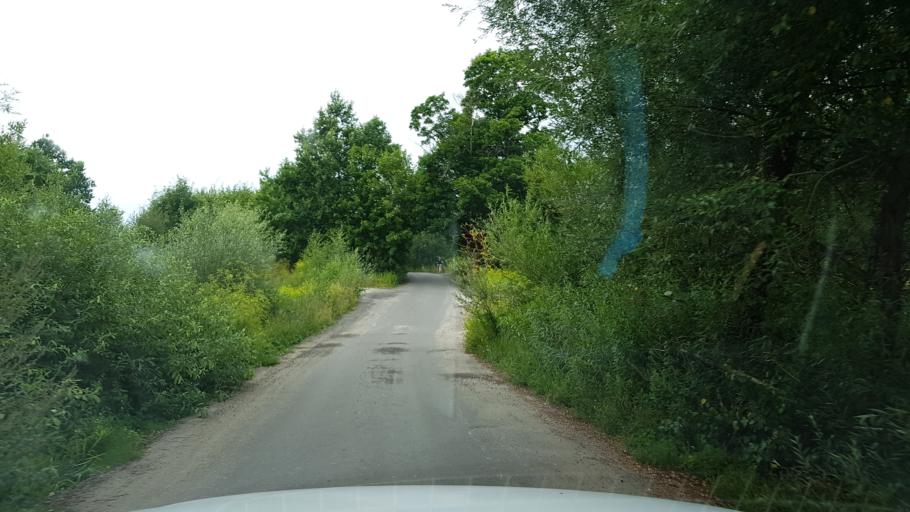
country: PL
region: West Pomeranian Voivodeship
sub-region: Powiat szczecinecki
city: Szczecinek
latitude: 53.6830
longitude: 16.6949
